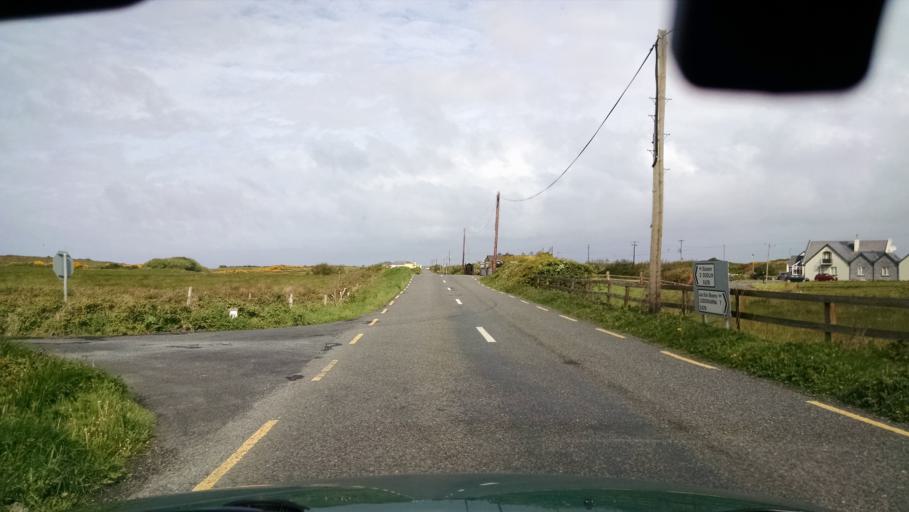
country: IE
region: Connaught
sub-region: County Galway
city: Bearna
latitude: 53.0108
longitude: -9.3647
